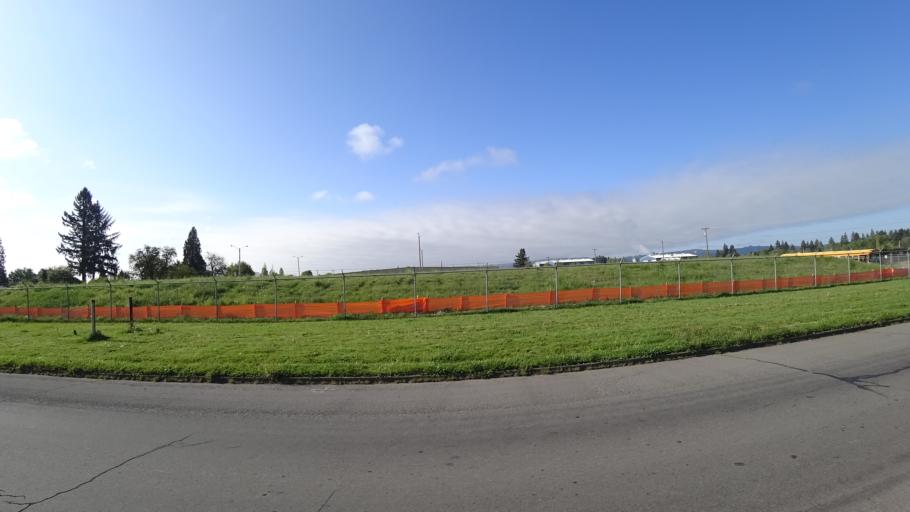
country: US
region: Oregon
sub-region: Washington County
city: Hillsboro
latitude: 45.5176
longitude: -122.9983
